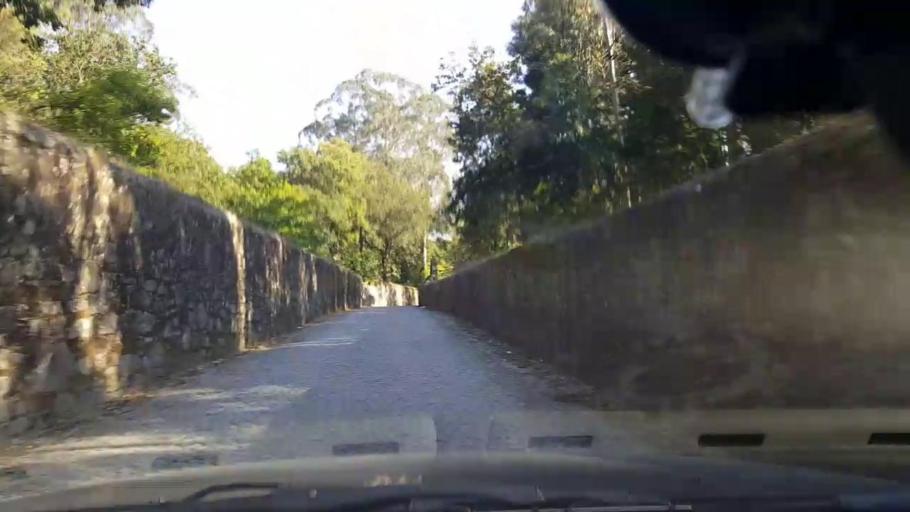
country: PT
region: Porto
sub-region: Vila do Conde
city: Arvore
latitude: 41.3440
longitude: -8.6884
